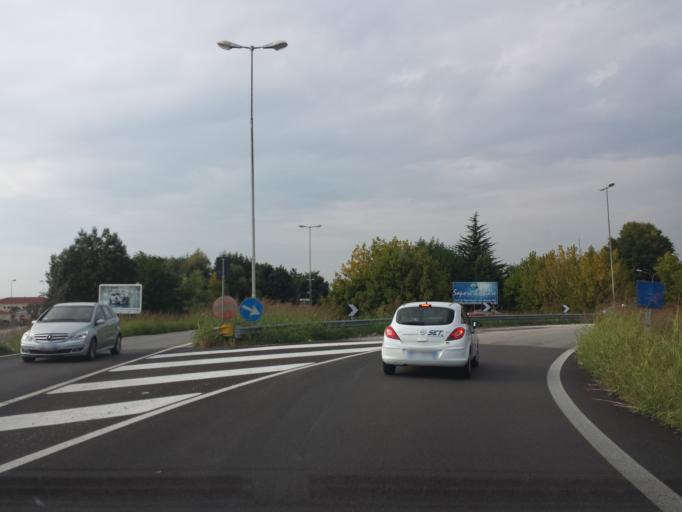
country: IT
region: Veneto
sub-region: Provincia di Vicenza
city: Villaggio Montegrappa
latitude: 45.5304
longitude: 11.5915
